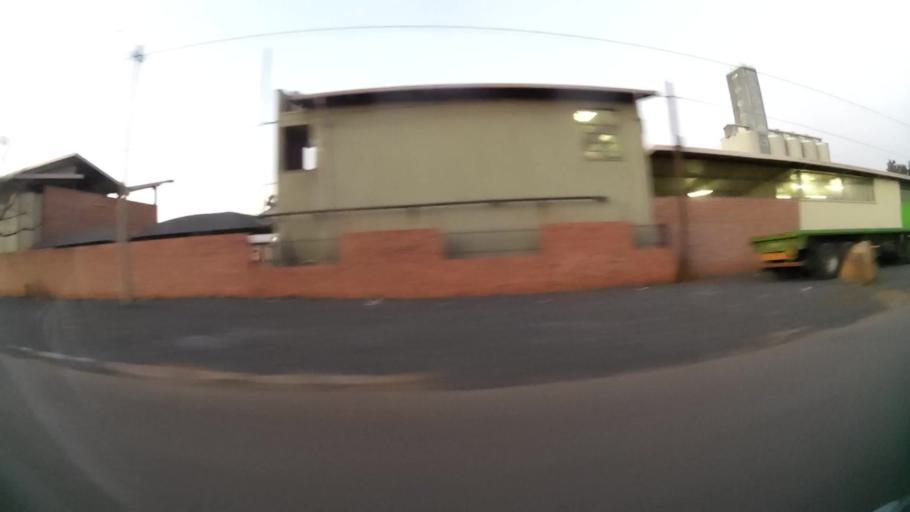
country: ZA
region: North-West
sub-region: Bojanala Platinum District Municipality
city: Rustenburg
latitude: -25.6763
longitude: 27.2555
